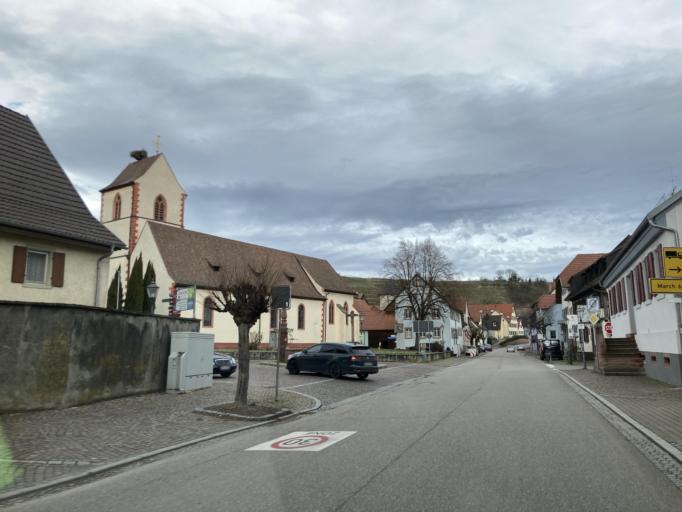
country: DE
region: Baden-Wuerttemberg
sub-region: Freiburg Region
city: Botzingen
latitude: 48.0768
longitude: 7.7254
